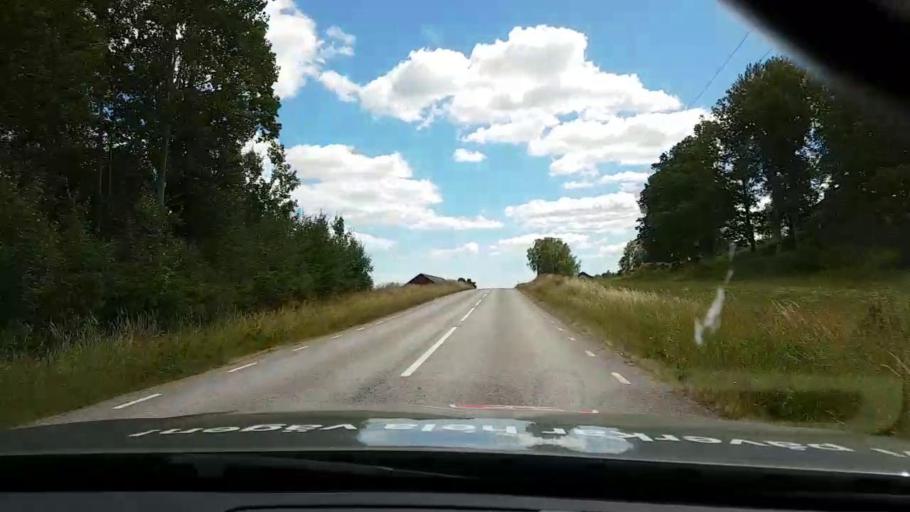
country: SE
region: Kalmar
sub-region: Vasterviks Kommun
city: Overum
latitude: 58.0487
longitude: 16.4095
